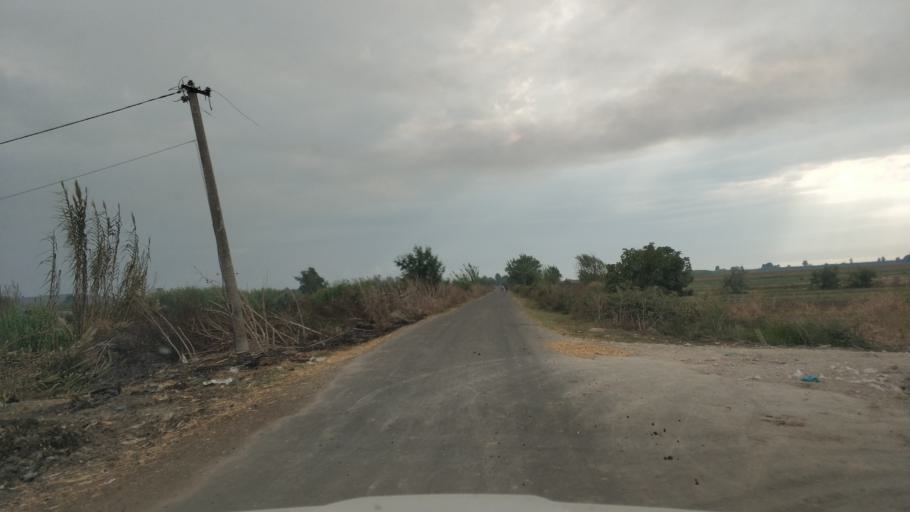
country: AL
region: Fier
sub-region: Rrethi i Fierit
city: Dermenas
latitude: 40.7292
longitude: 19.4643
